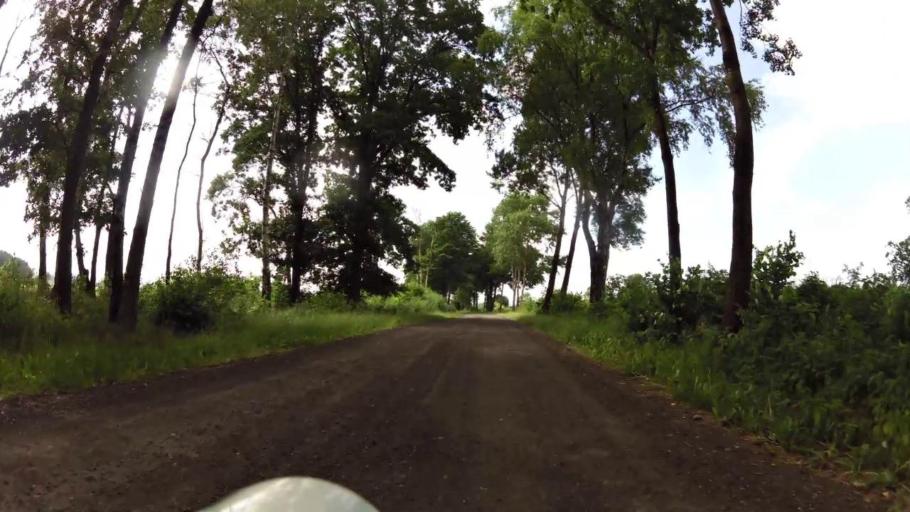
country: PL
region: West Pomeranian Voivodeship
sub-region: Powiat koszalinski
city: Bobolice
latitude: 53.9506
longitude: 16.6264
